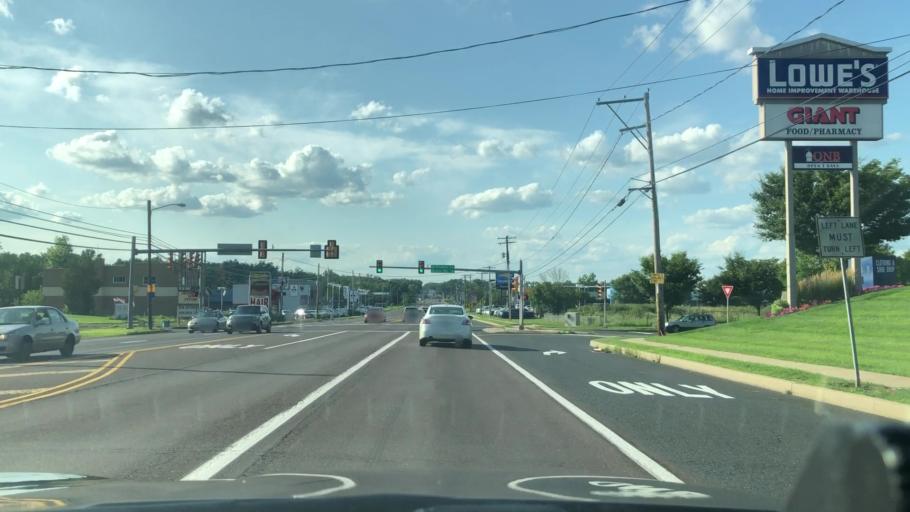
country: US
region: Pennsylvania
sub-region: Bucks County
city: Quakertown
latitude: 40.4210
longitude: -75.3457
